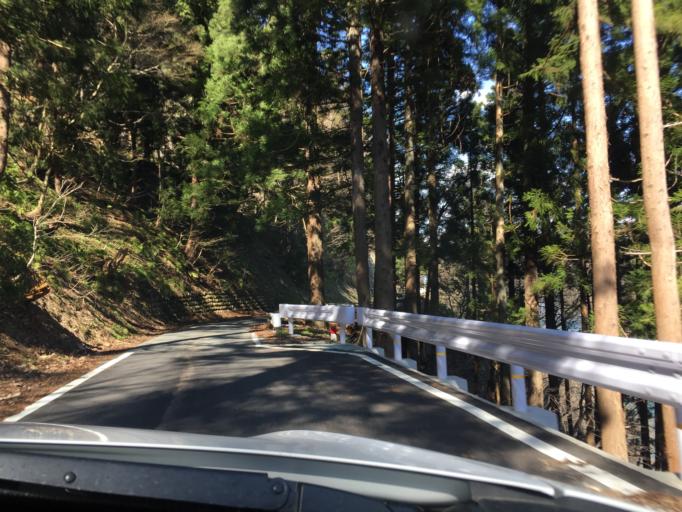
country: JP
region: Yamagata
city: Nagai
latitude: 38.2640
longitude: 140.1075
